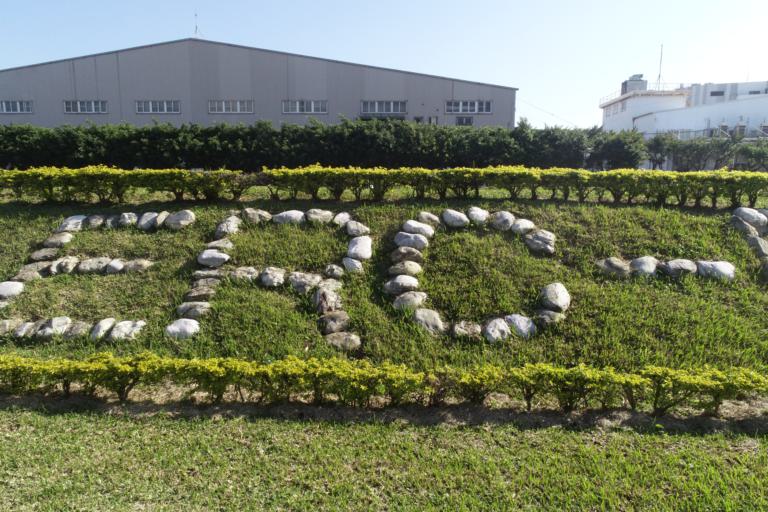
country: TW
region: Taiwan
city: Taoyuan City
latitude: 24.9851
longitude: 121.2401
